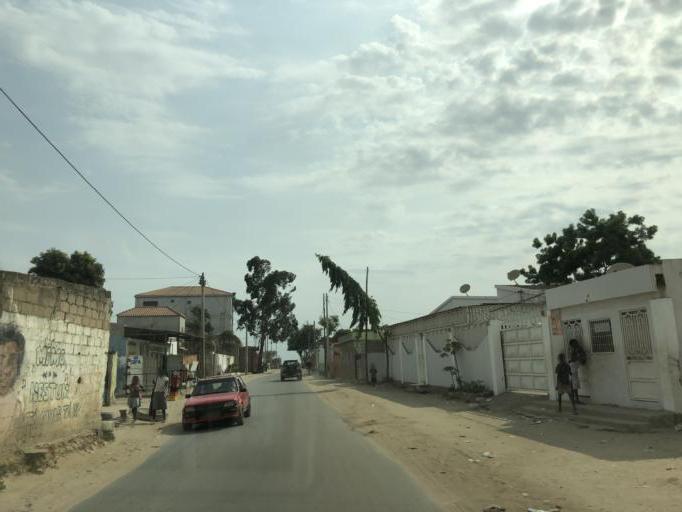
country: AO
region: Luanda
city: Luanda
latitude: -8.8972
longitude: 13.3510
